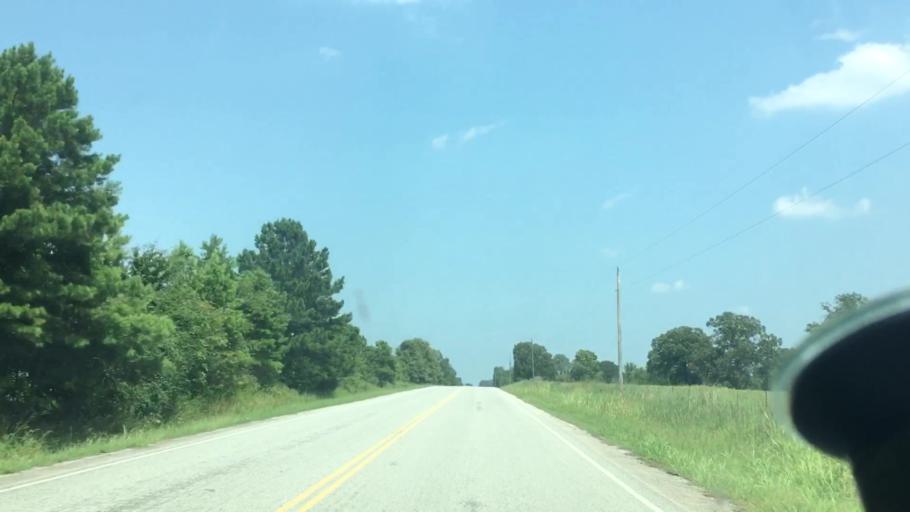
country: US
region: Oklahoma
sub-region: Atoka County
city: Atoka
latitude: 34.2655
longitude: -95.9361
